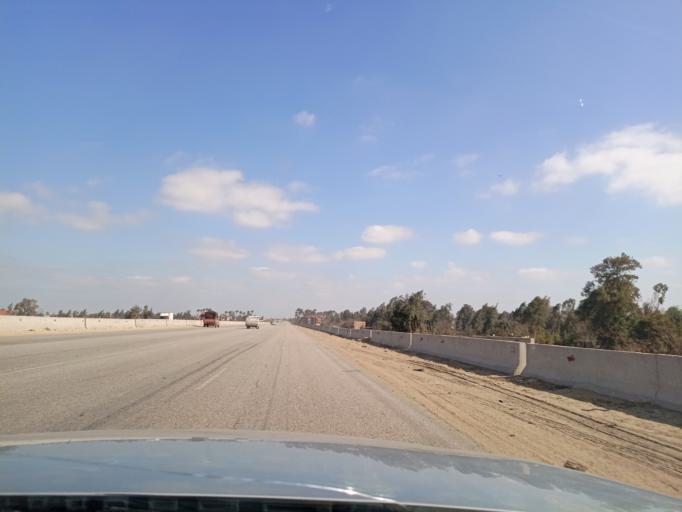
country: EG
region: Muhafazat al Qalyubiyah
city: Banha
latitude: 30.4418
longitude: 31.1146
